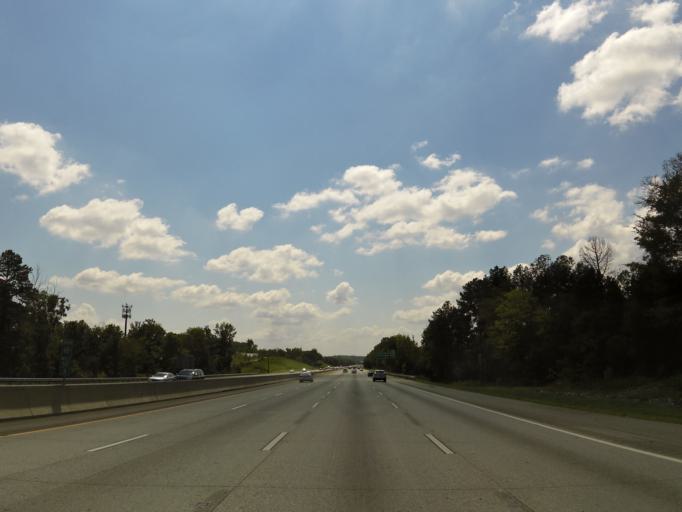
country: US
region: North Carolina
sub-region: Cabarrus County
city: Harrisburg
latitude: 35.3883
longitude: -80.7037
